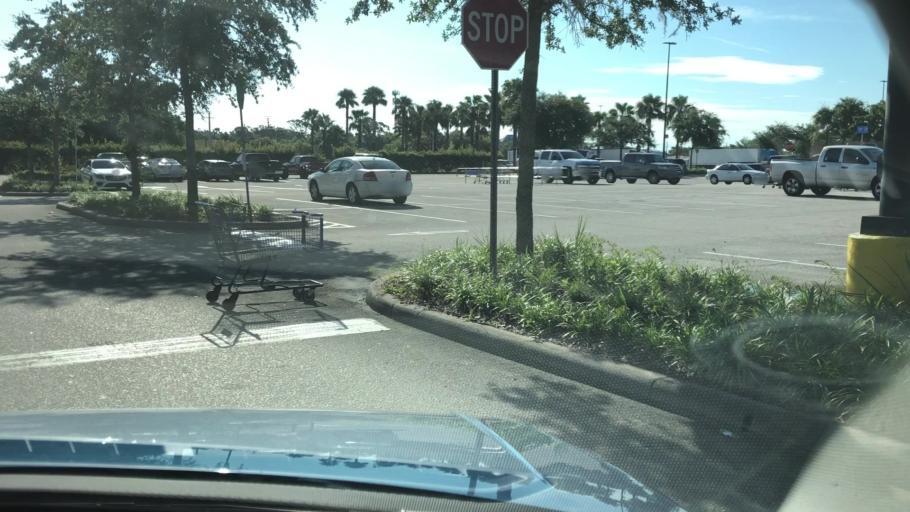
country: US
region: Florida
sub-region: Volusia County
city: South Daytona
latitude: 29.1741
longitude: -81.0301
